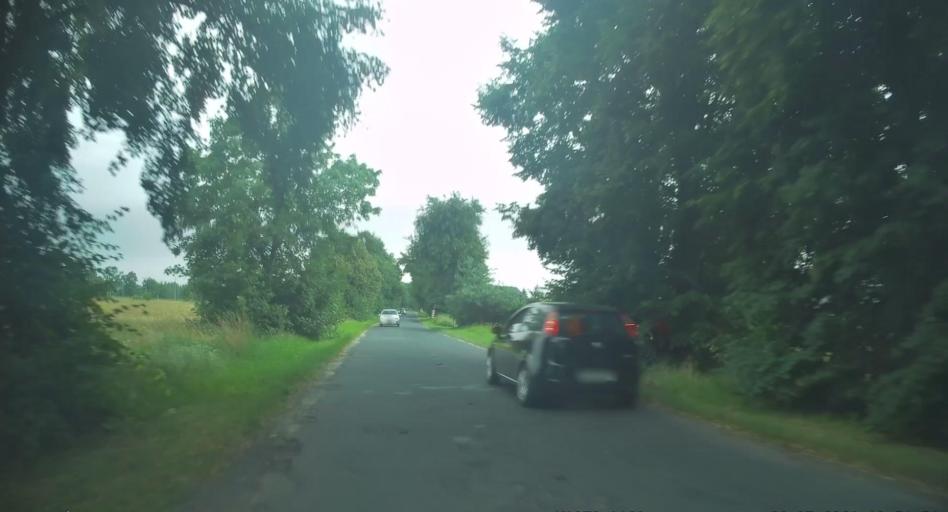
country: PL
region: Lodz Voivodeship
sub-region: Powiat rawski
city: Rawa Mazowiecka
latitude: 51.7522
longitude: 20.1879
